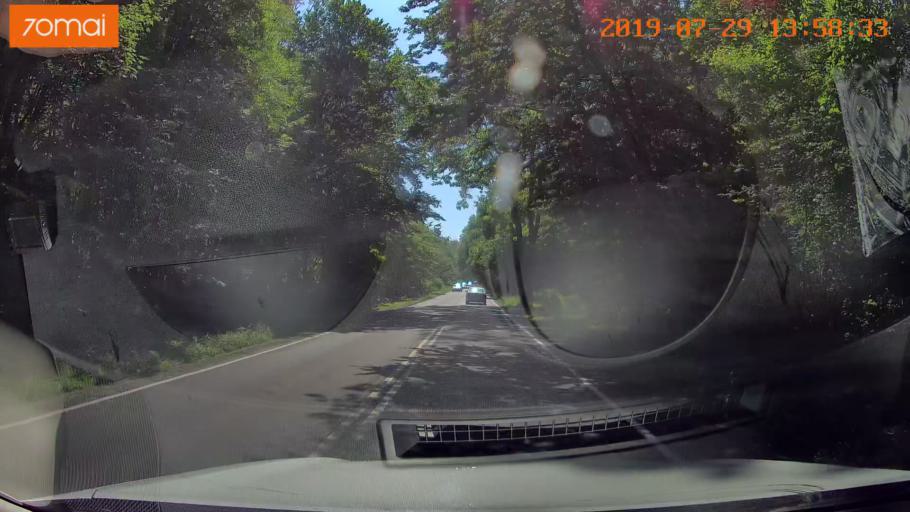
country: RU
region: Kaliningrad
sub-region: Gorod Kaliningrad
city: Baltiysk
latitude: 54.6925
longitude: 19.9362
